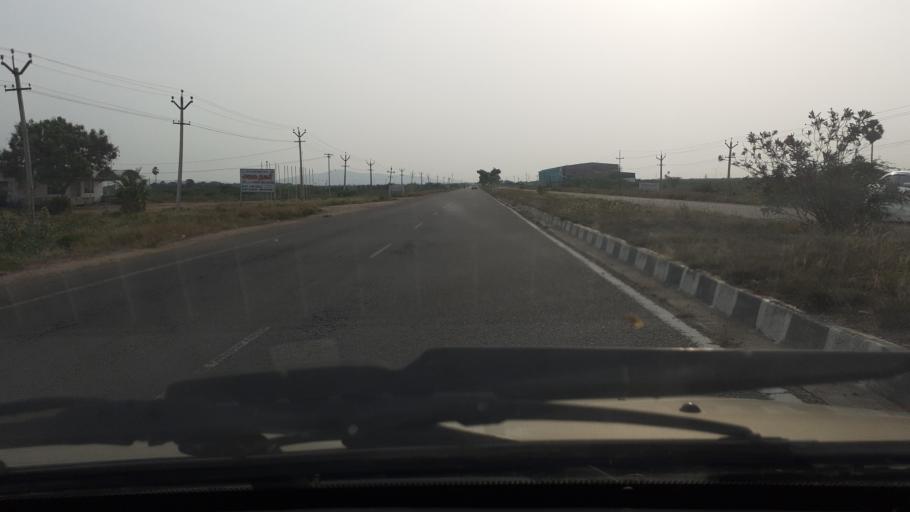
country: IN
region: Tamil Nadu
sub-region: Thoothukkudi
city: Korampallam
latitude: 8.7345
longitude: 77.9834
